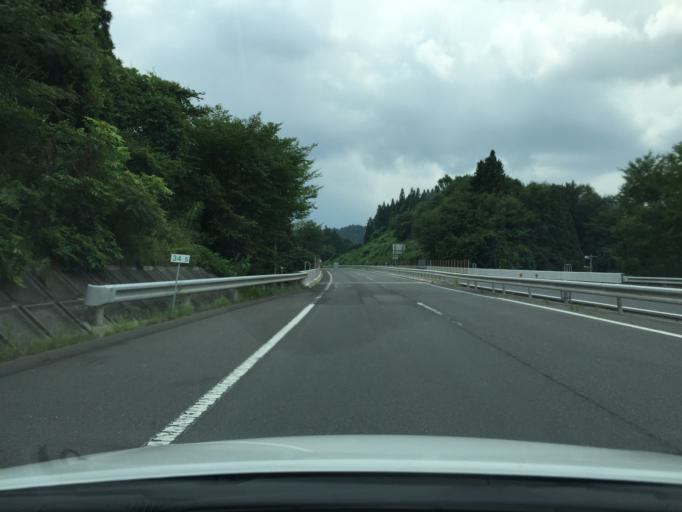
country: JP
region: Fukushima
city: Funehikimachi-funehiki
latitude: 37.2847
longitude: 140.6144
